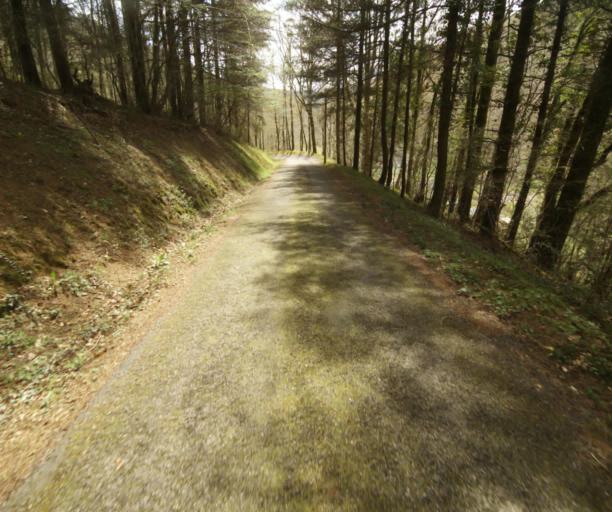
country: FR
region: Limousin
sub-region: Departement de la Correze
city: Sainte-Fortunade
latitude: 45.1874
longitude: 1.8759
